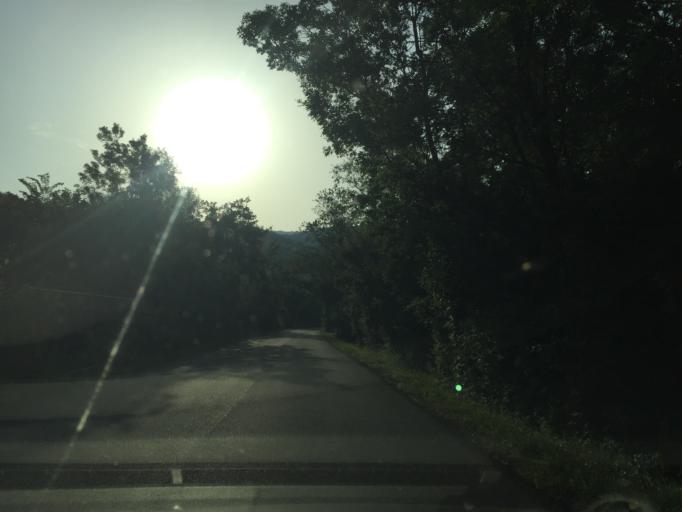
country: IT
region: Friuli Venezia Giulia
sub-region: Provincia di Trieste
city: Domio
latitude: 45.5883
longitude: 13.8279
